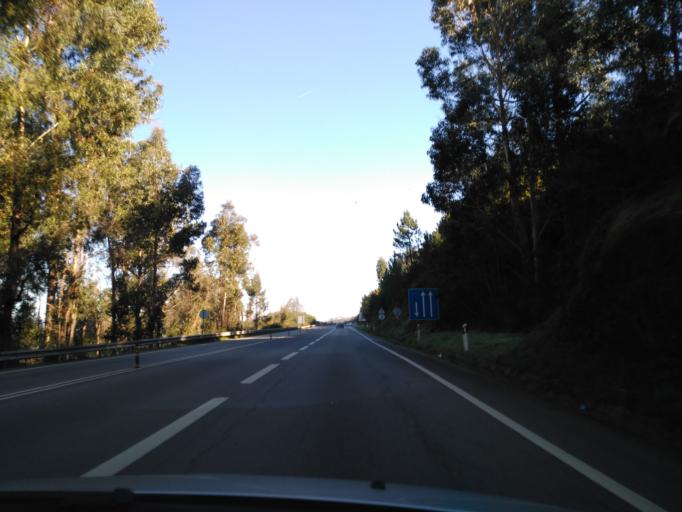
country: PT
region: Braga
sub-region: Braga
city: Adaufe
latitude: 41.5844
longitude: -8.3684
